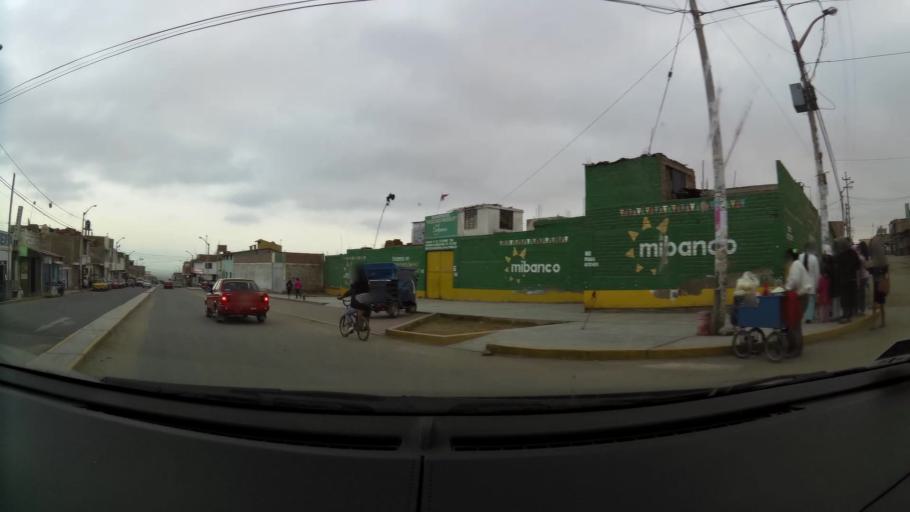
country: PE
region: La Libertad
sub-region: Provincia de Trujillo
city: La Esperanza
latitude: -8.0674
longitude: -79.0218
